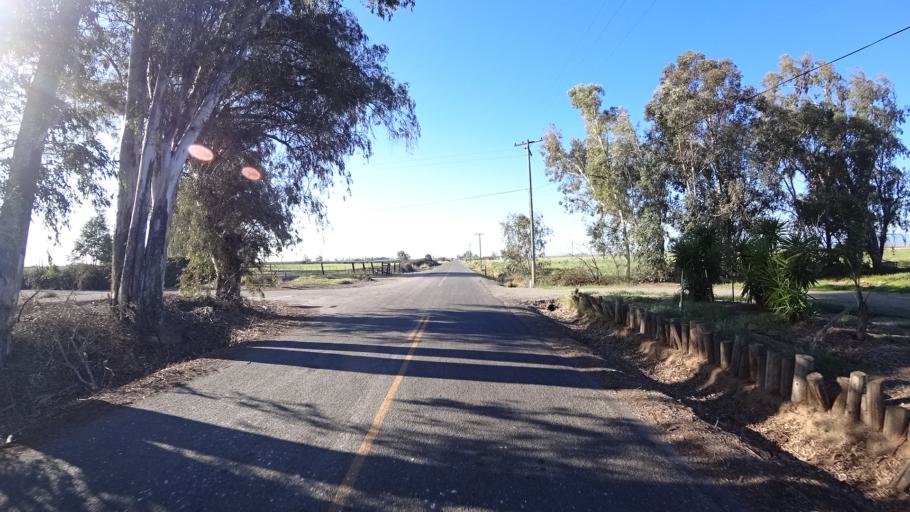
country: US
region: California
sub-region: Glenn County
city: Orland
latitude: 39.7554
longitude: -122.2479
